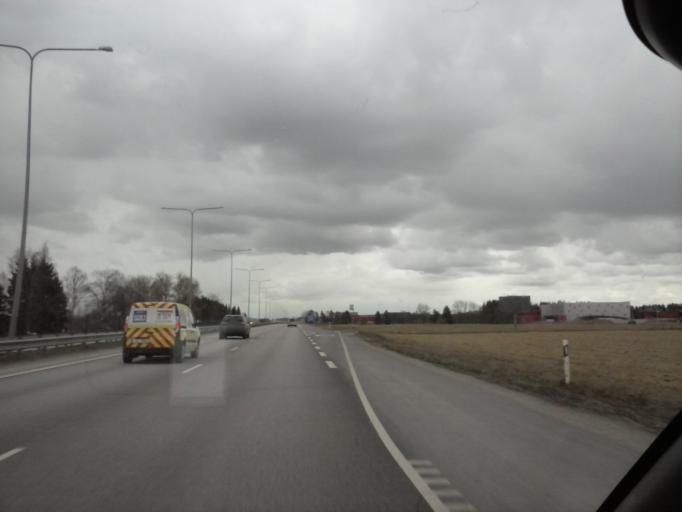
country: EE
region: Harju
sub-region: Rae vald
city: Jueri
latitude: 59.3901
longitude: 24.8280
